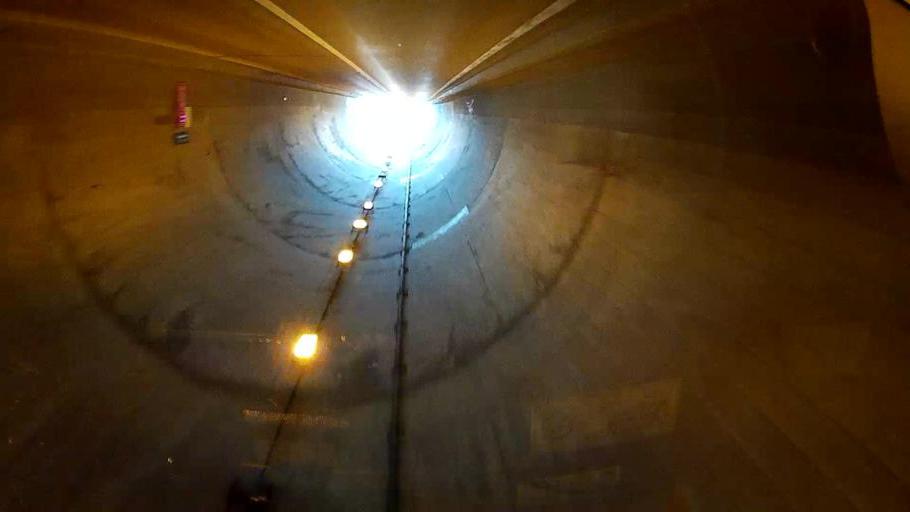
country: JP
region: Nagano
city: Toyoshina
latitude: 36.1785
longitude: 137.7820
